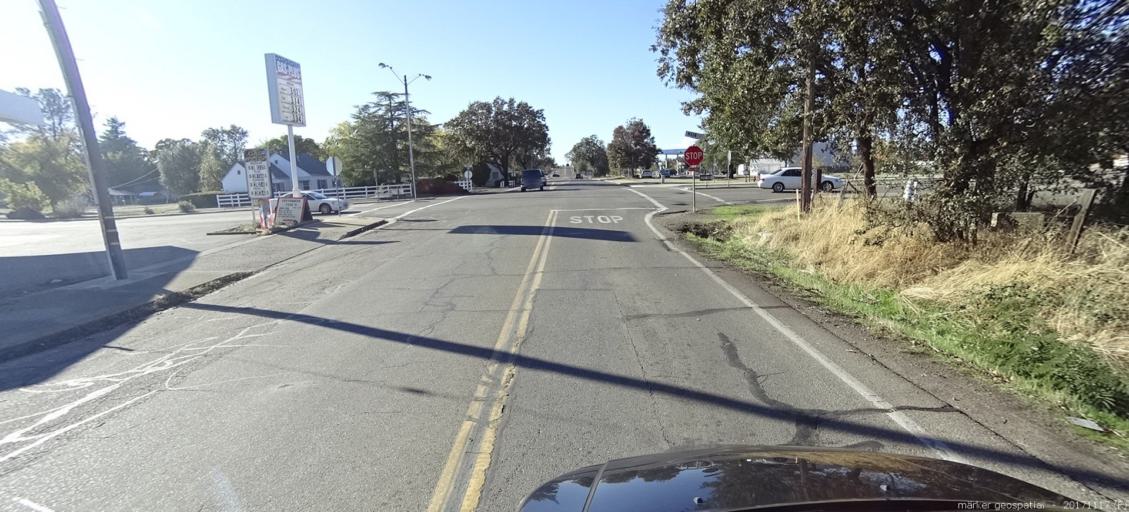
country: US
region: California
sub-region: Shasta County
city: Cottonwood
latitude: 40.3894
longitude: -122.2804
